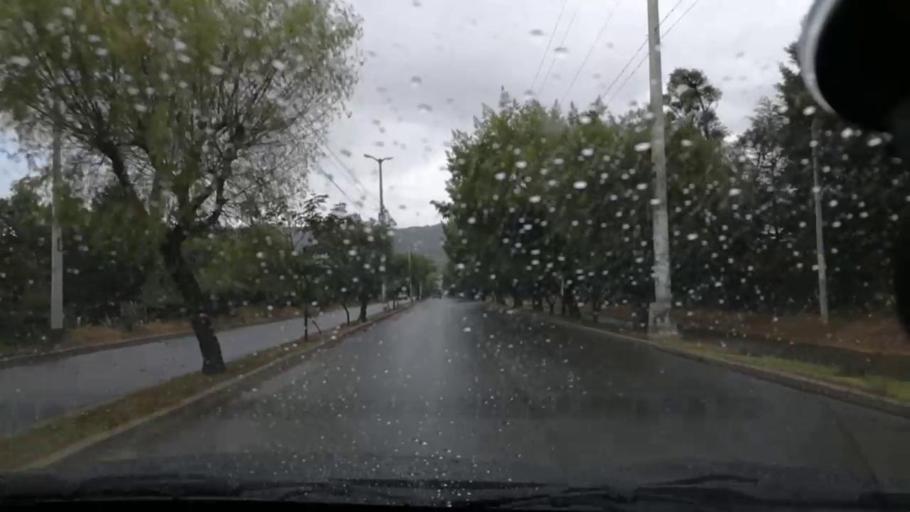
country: PE
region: Cajamarca
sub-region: Provincia de Cajamarca
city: Cajamarca
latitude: -7.1653
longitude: -78.4879
